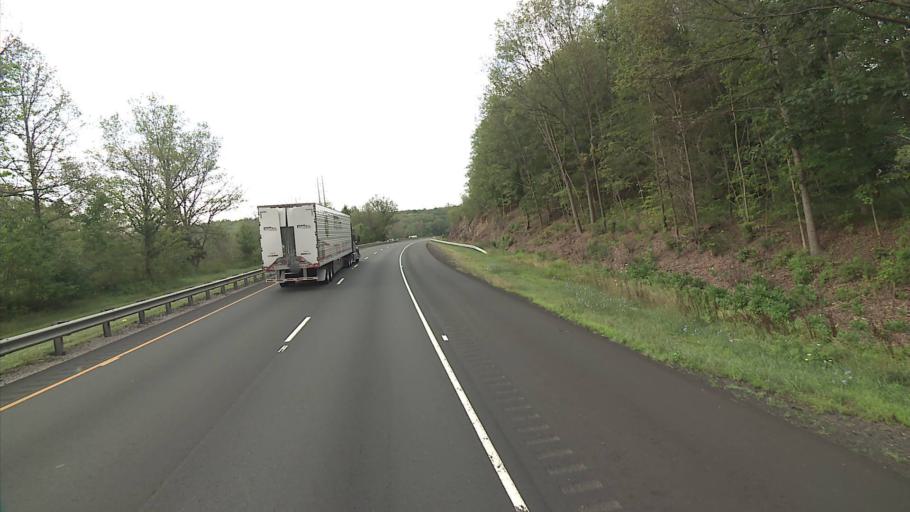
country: US
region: Connecticut
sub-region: New Haven County
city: Middlebury
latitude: 41.5275
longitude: -73.0885
